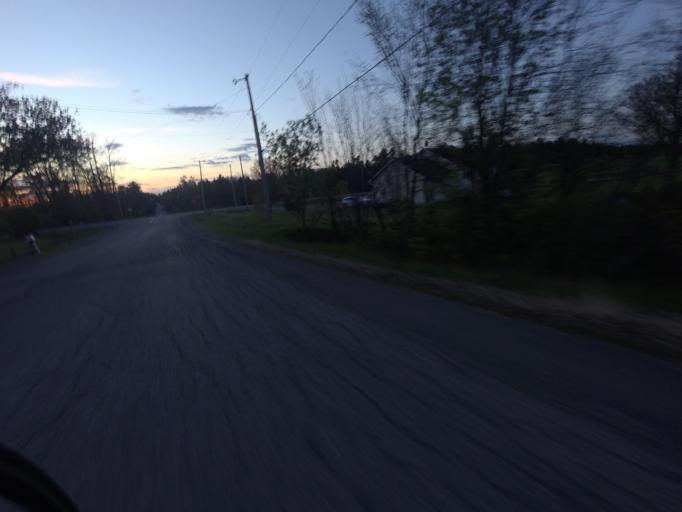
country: CA
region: Ontario
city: Arnprior
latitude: 45.4322
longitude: -76.2412
